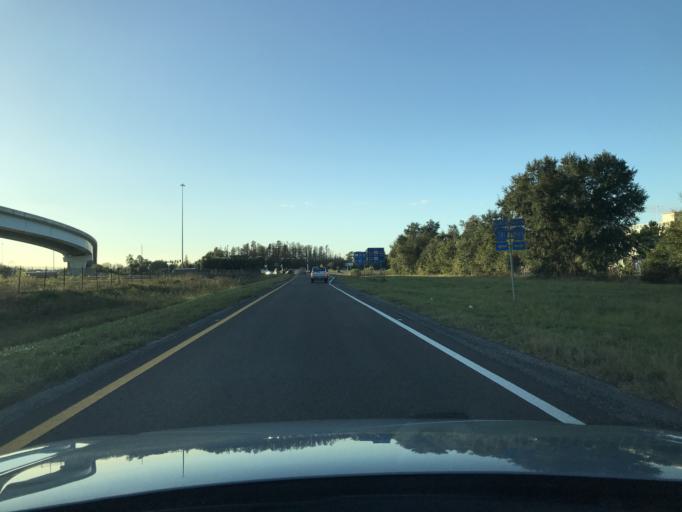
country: US
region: Florida
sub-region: Hillsborough County
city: Pebble Creek
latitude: 28.1230
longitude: -82.3758
